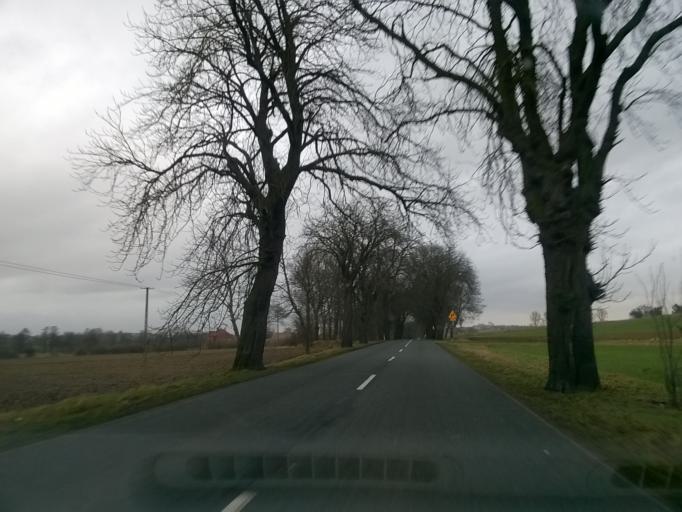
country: PL
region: Kujawsko-Pomorskie
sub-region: Powiat nakielski
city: Kcynia
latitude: 52.9751
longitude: 17.4534
